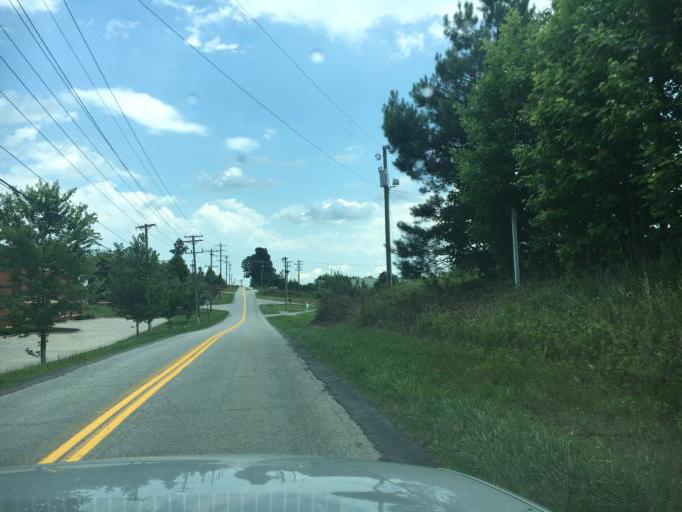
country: US
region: South Carolina
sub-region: Greenville County
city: Greer
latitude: 34.8739
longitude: -82.2353
